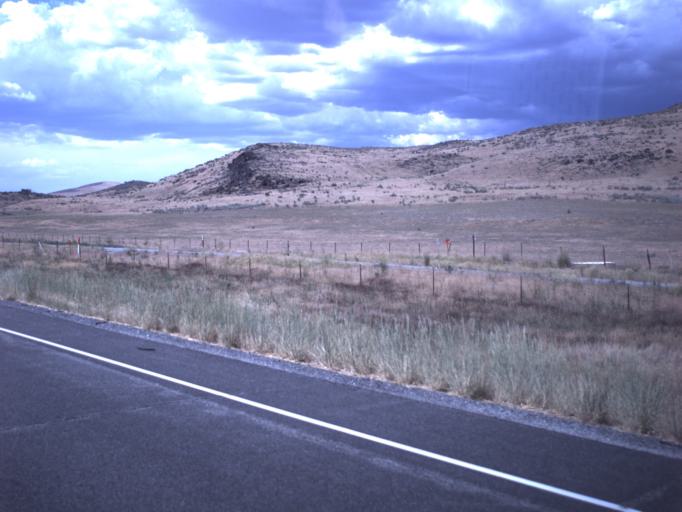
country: US
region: Idaho
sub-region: Oneida County
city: Malad City
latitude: 41.9004
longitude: -112.5795
